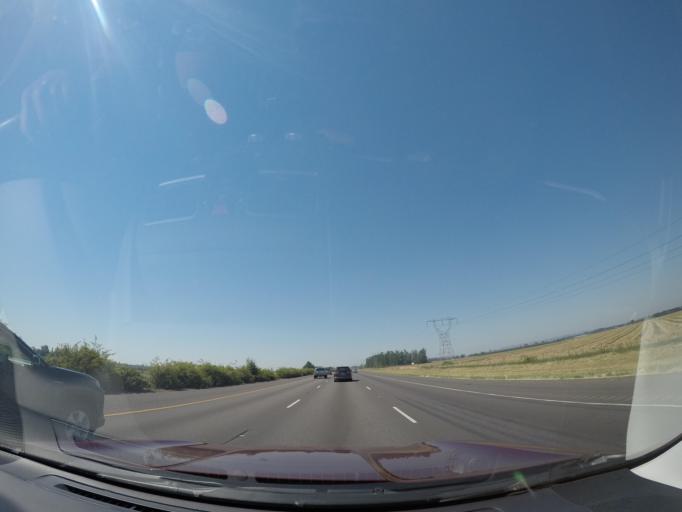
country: US
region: Oregon
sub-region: Marion County
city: Gervais
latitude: 45.1312
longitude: -122.9012
